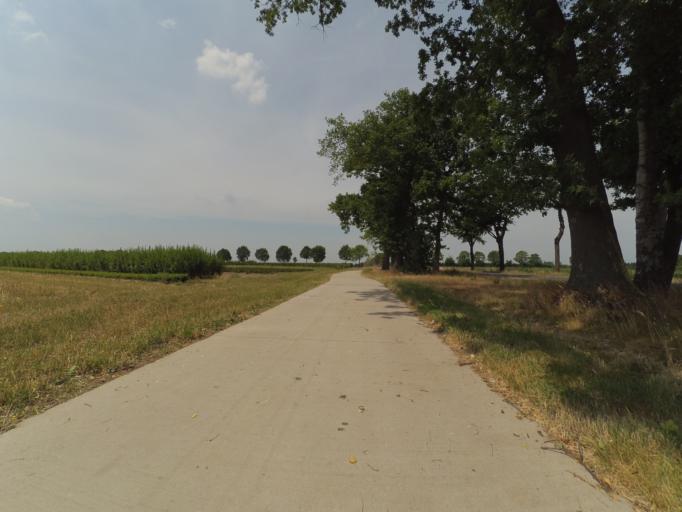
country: BE
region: Flanders
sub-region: Provincie Antwerpen
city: Wuustwezel
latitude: 51.4096
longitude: 4.5363
